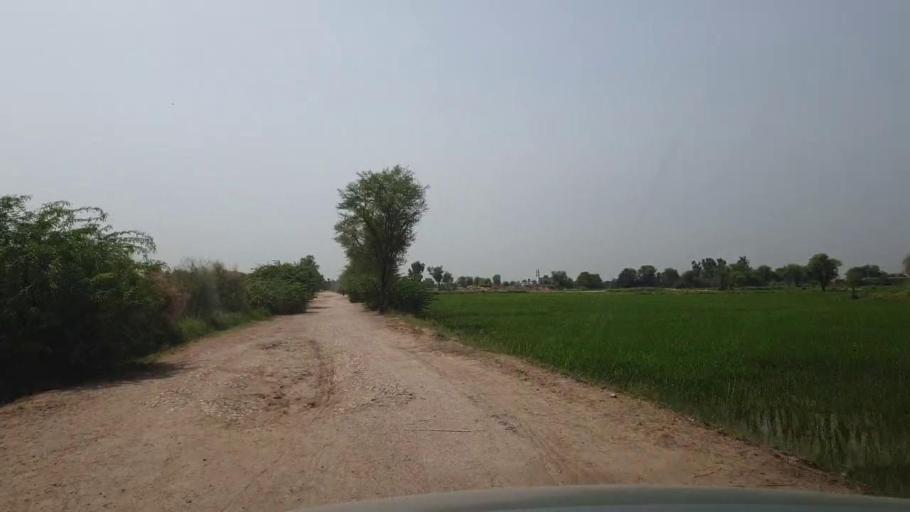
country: PK
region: Sindh
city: Madeji
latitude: 27.8054
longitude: 68.5375
